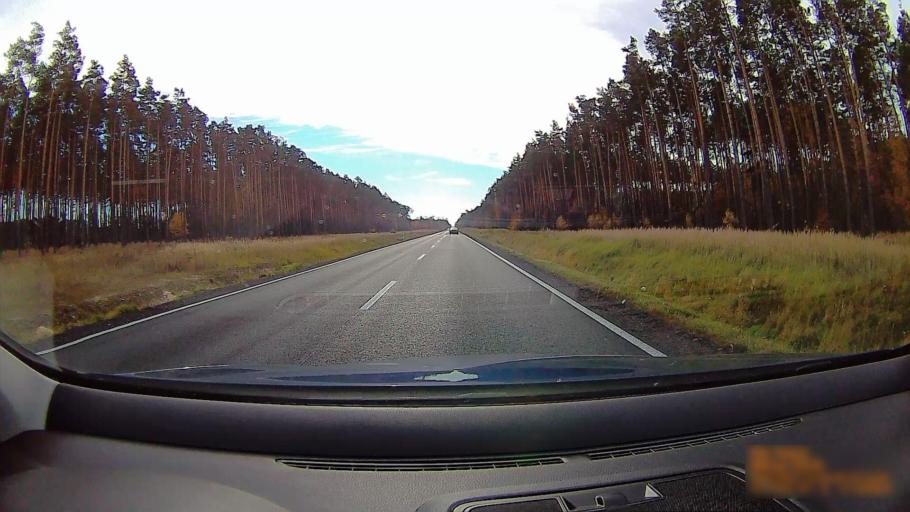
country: PL
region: Greater Poland Voivodeship
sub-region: Powiat ostrowski
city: Przygodzice
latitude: 51.5506
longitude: 17.8470
